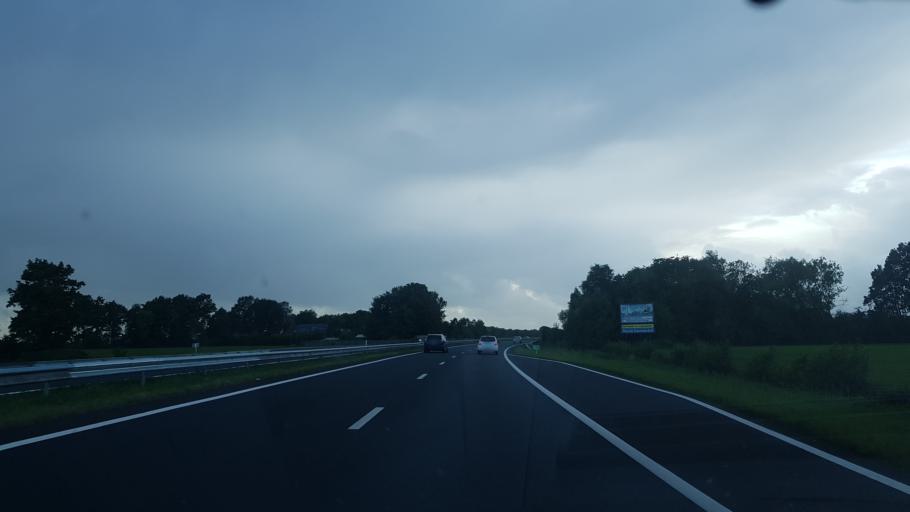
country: NL
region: Friesland
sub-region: Gemeente Smallingerland
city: Oudega
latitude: 53.1452
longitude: 5.9960
